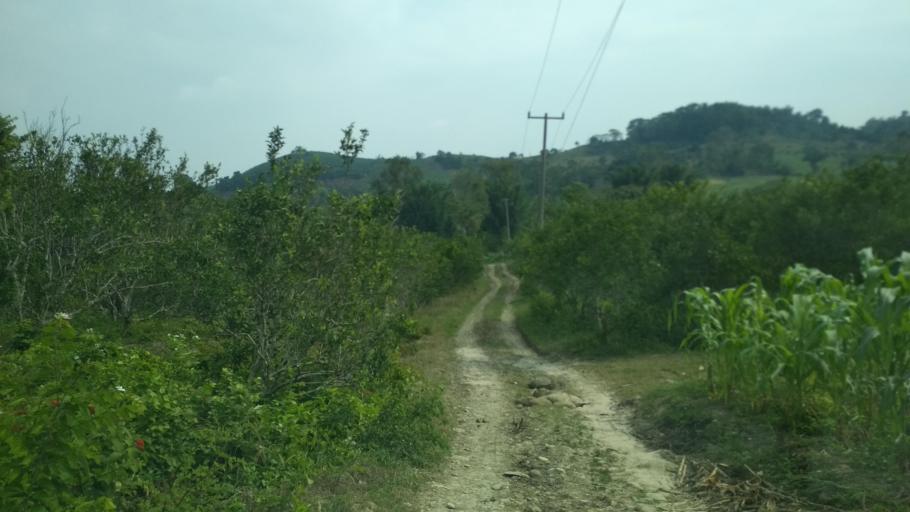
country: MM
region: Kayah
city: Loikaw
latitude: 20.2047
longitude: 97.3196
